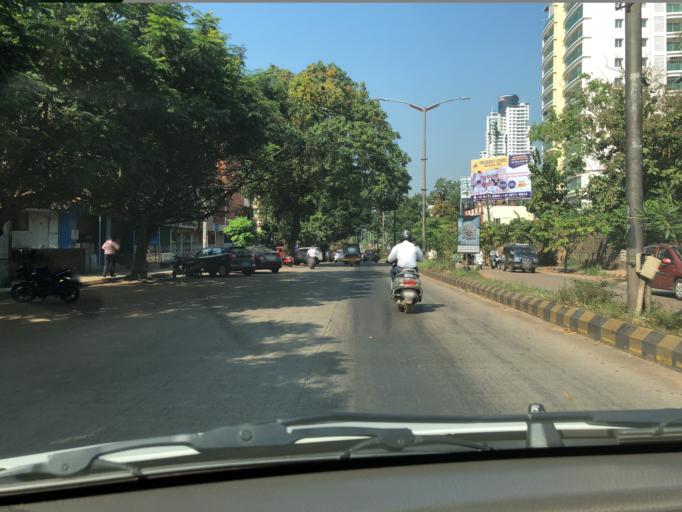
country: IN
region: Karnataka
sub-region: Dakshina Kannada
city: Mangalore
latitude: 12.8899
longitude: 74.8352
